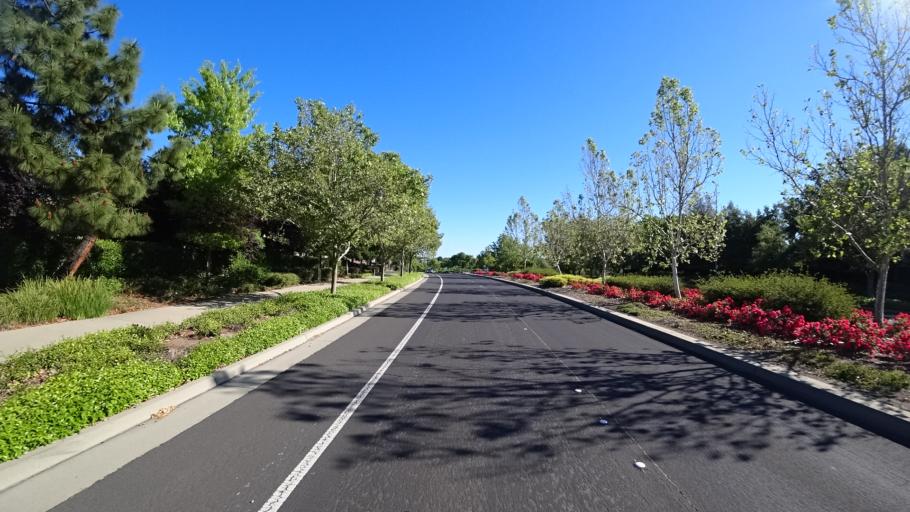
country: US
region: California
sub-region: Placer County
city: Rocklin
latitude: 38.7951
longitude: -121.2768
